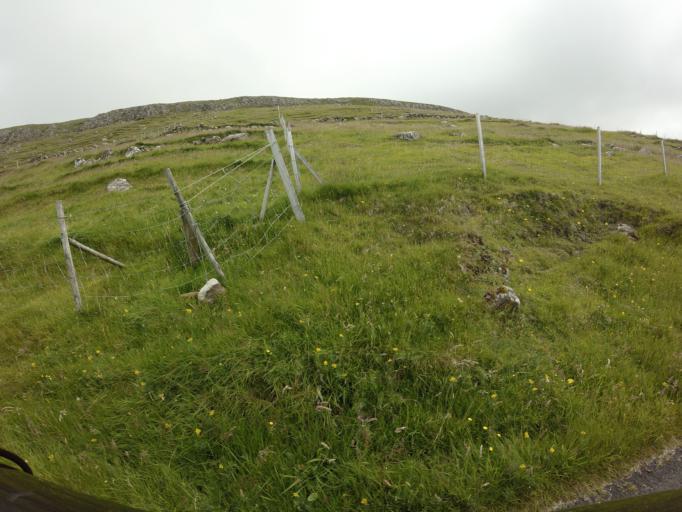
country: FO
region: Sandoy
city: Sandur
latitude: 61.7980
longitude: -6.7515
